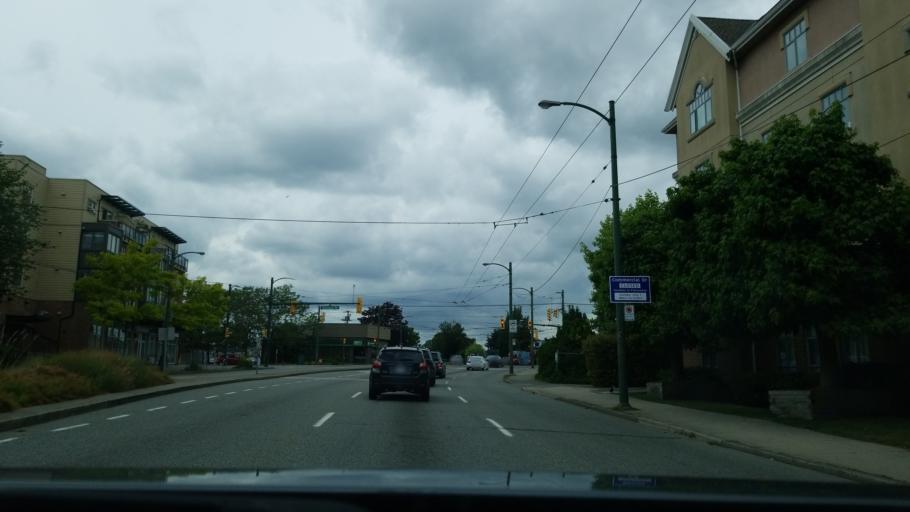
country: CA
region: British Columbia
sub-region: Fraser Valley Regional District
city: North Vancouver
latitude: 49.2621
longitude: -123.0553
